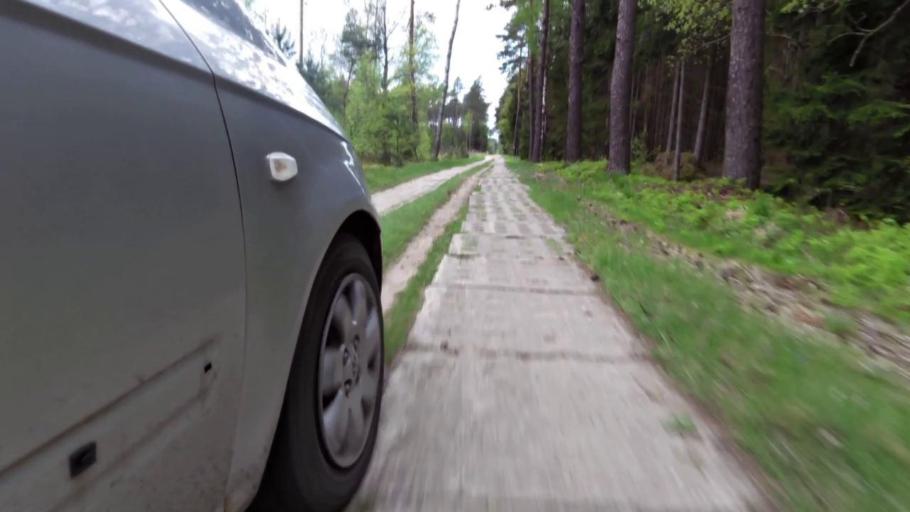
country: PL
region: West Pomeranian Voivodeship
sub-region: Powiat walecki
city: Walcz
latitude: 53.2714
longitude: 16.3726
